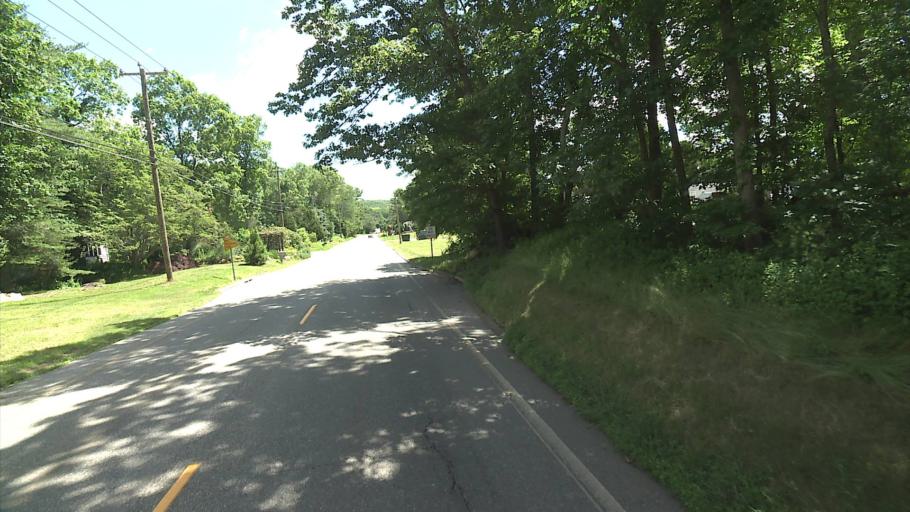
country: US
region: Connecticut
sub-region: New London County
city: Pawcatuck
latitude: 41.4214
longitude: -71.8912
